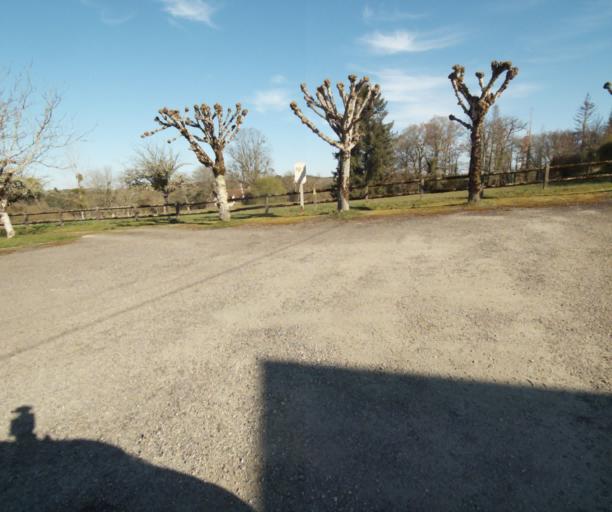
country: FR
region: Limousin
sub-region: Departement de la Correze
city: Correze
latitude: 45.3016
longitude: 1.8685
